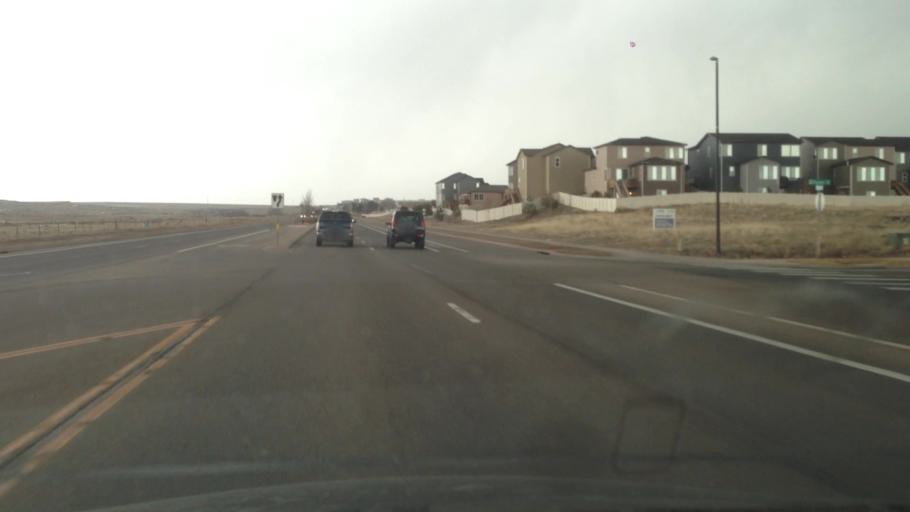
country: US
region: Colorado
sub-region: Douglas County
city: Parker
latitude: 39.4931
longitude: -104.7789
